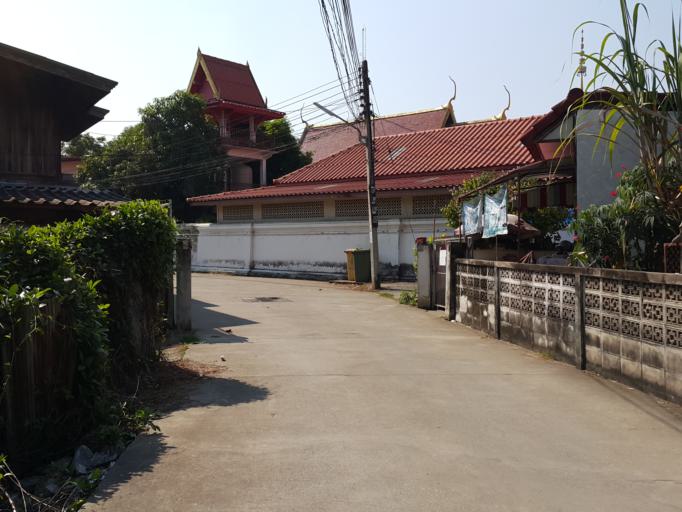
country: TH
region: Lampang
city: Lampang
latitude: 18.2977
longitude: 99.5085
